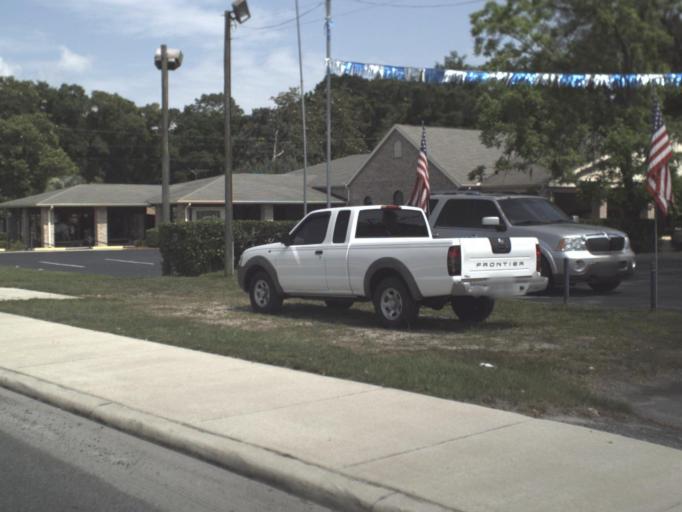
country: US
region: Florida
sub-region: Putnam County
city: Palatka
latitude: 29.6416
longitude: -81.6618
